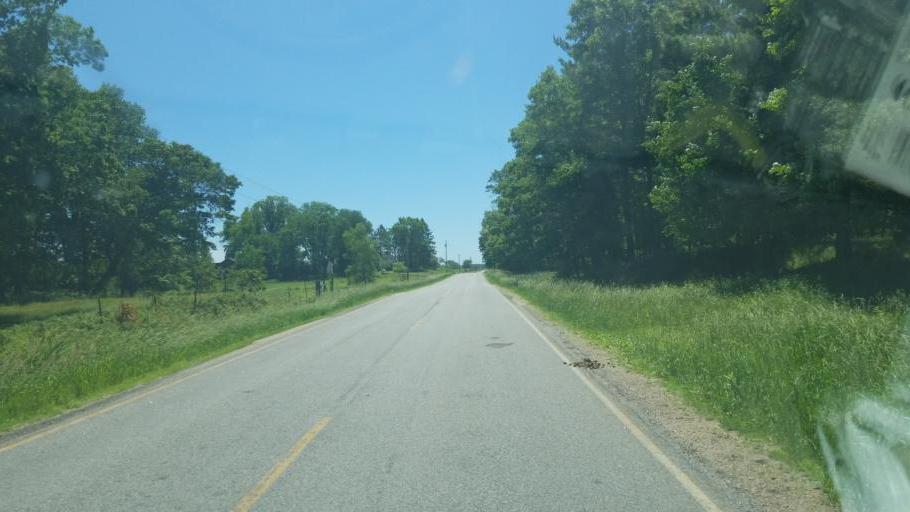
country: US
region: Wisconsin
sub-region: Juneau County
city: New Lisbon
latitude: 44.0203
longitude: -90.2718
